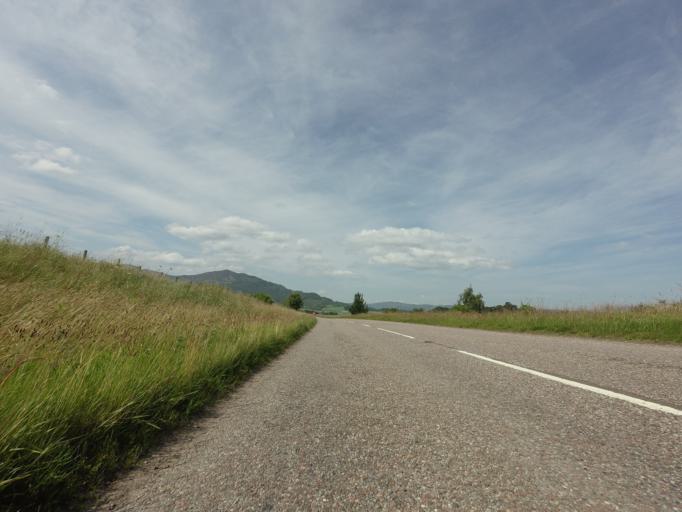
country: GB
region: Scotland
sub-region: Highland
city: Tain
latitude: 57.8378
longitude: -4.1854
